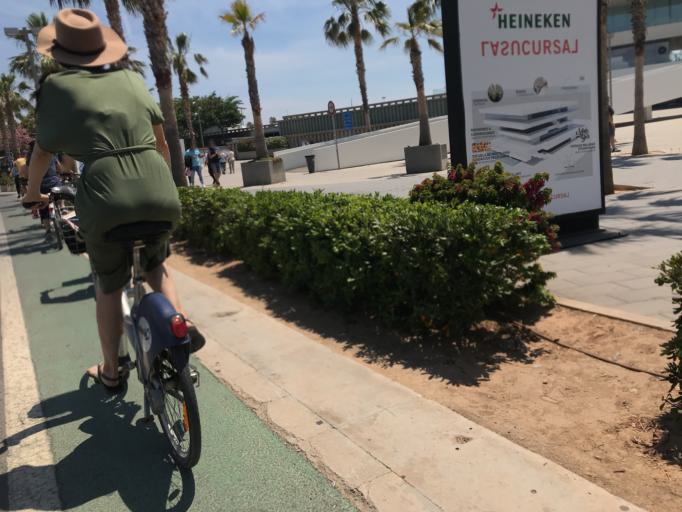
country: ES
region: Valencia
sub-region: Provincia de Valencia
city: Alboraya
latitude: 39.4621
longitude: -0.3249
